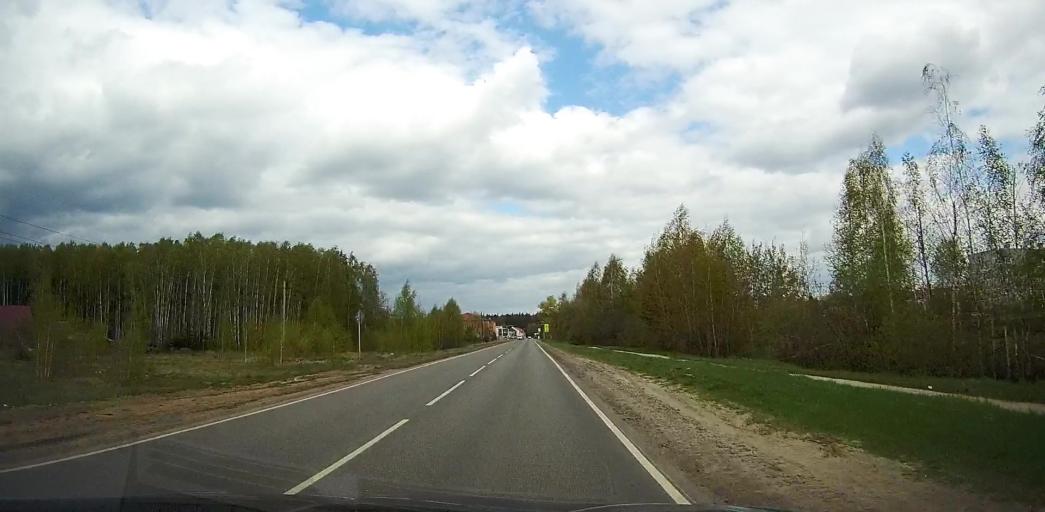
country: RU
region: Moskovskaya
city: Ashitkovo
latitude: 55.4335
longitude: 38.5785
